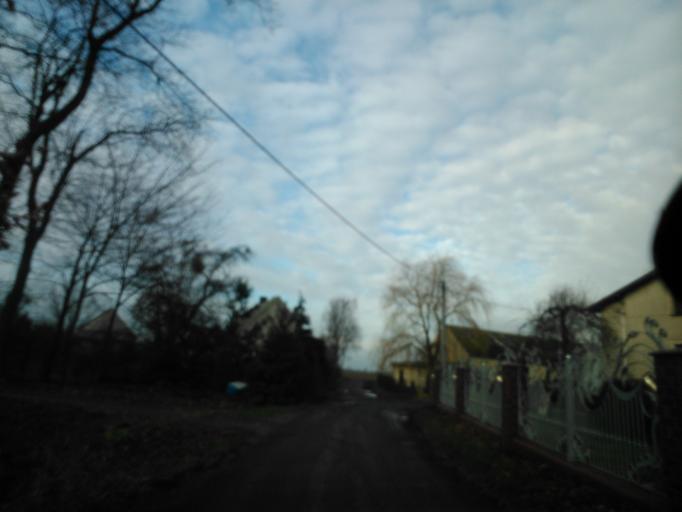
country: PL
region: Kujawsko-Pomorskie
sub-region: Powiat wabrzeski
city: Debowa Laka
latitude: 53.2235
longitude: 19.1254
